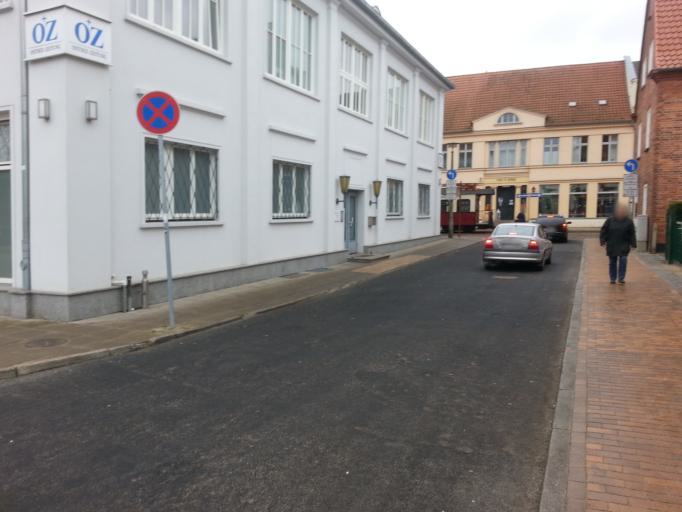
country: DE
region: Mecklenburg-Vorpommern
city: Bad Doberan
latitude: 54.1049
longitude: 11.9025
